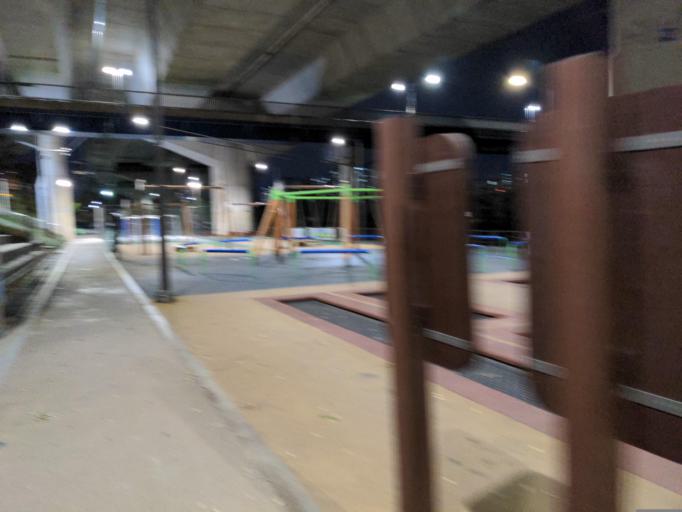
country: KR
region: Seoul
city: Seoul
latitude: 37.5616
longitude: 127.0493
